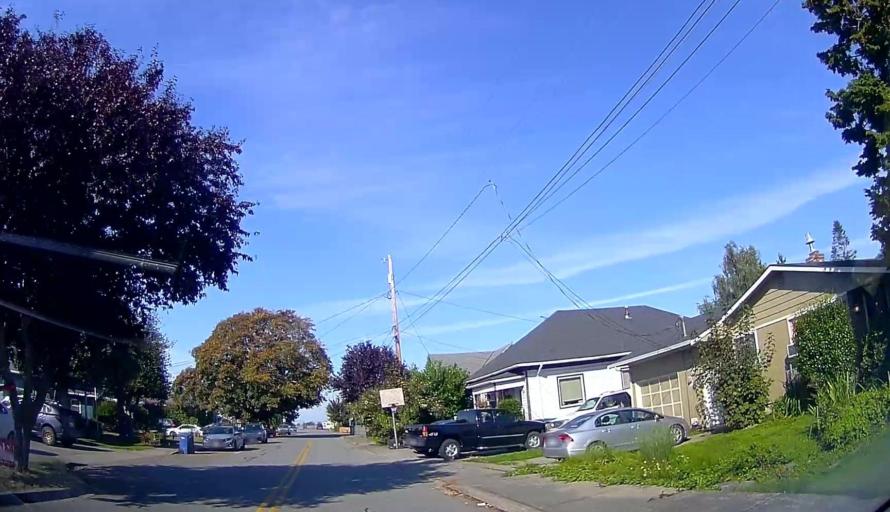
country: US
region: Washington
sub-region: Snohomish County
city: Stanwood
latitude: 48.2429
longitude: -122.3741
